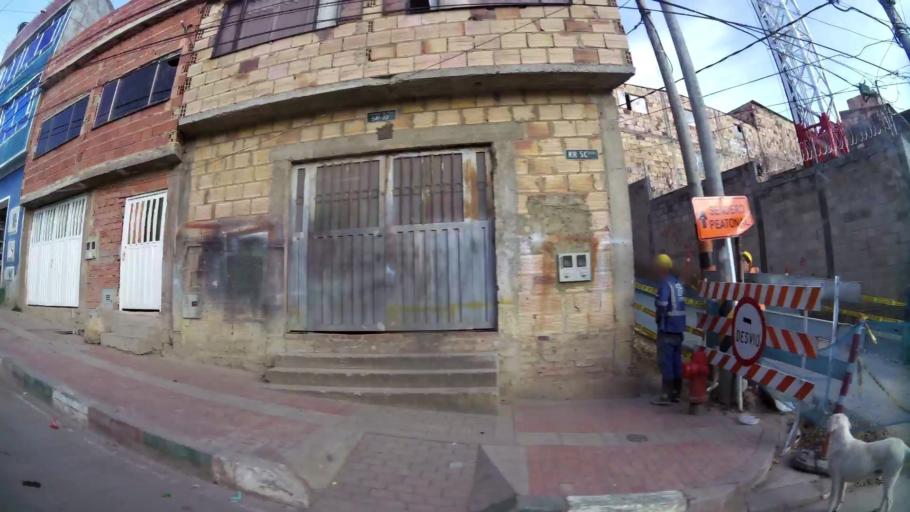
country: CO
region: Bogota D.C.
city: Bogota
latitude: 4.5356
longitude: -74.0930
